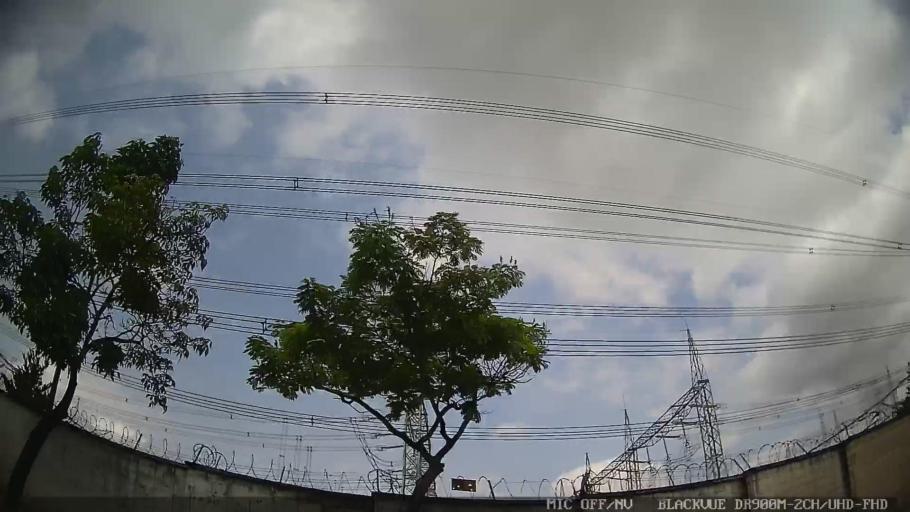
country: BR
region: Sao Paulo
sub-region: Taboao Da Serra
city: Taboao da Serra
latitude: -23.6574
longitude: -46.7246
